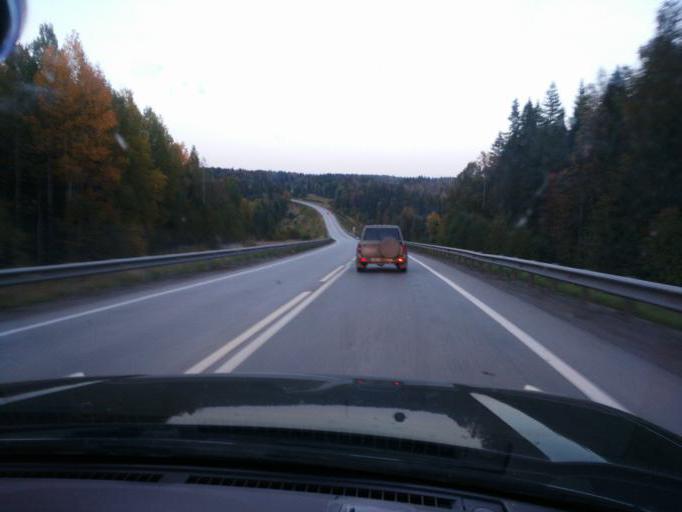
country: RU
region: Perm
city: Novyye Lyady
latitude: 58.2834
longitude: 56.7214
